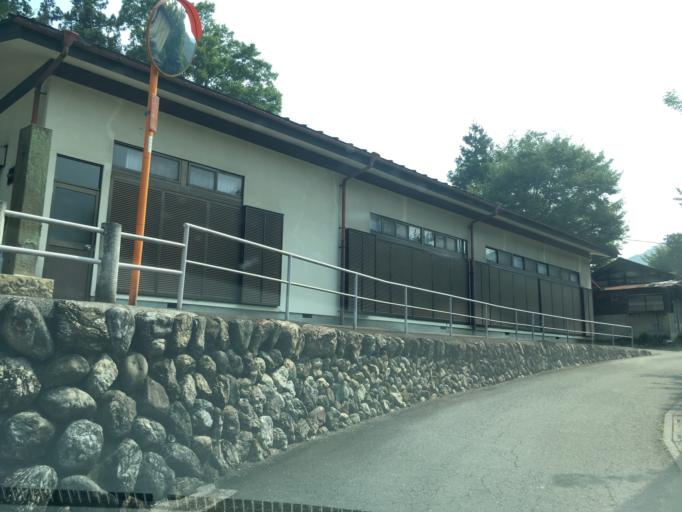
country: JP
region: Saitama
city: Chichibu
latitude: 36.0045
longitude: 139.1068
